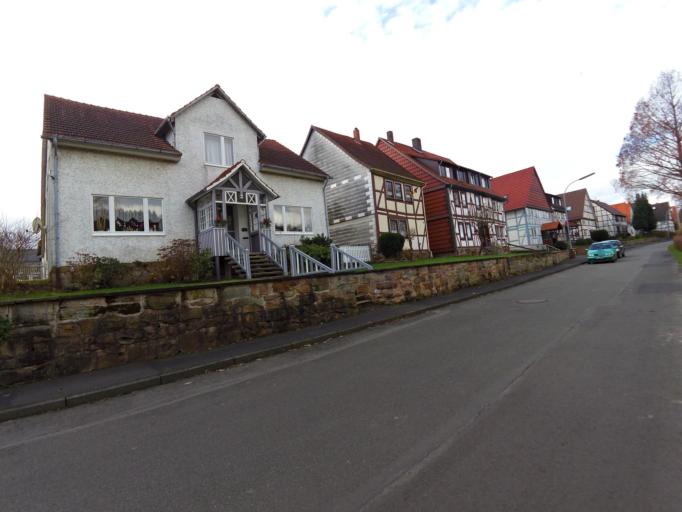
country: DE
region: Lower Saxony
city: Buhren
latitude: 51.4804
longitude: 9.6188
